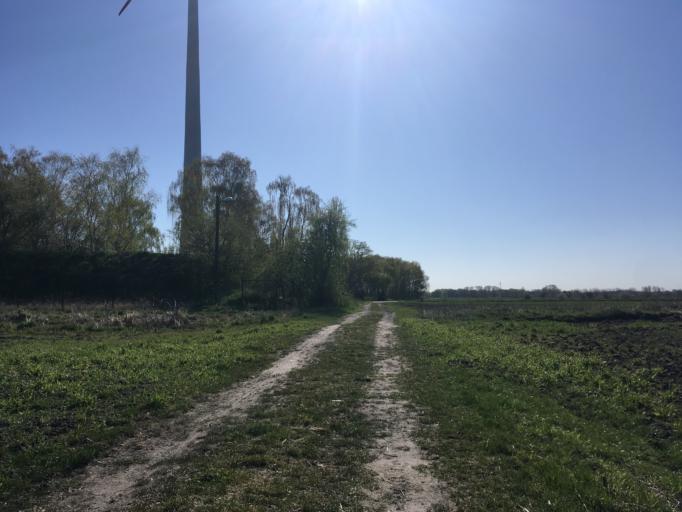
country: DE
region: Berlin
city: Buchholz
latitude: 52.6302
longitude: 13.4407
